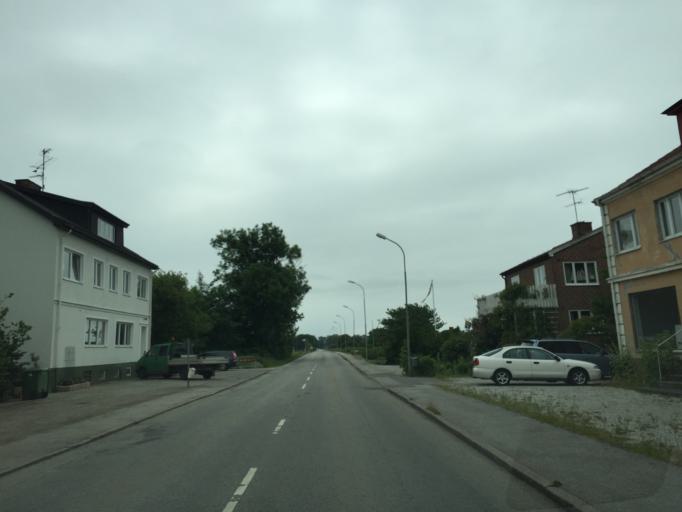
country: SE
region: Skane
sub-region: Ystads Kommun
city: Kopingebro
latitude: 55.4356
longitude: 14.1136
